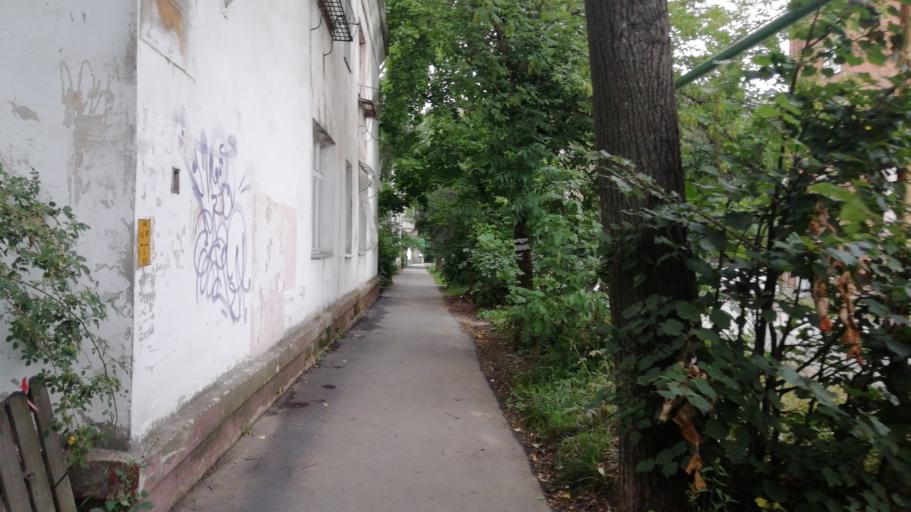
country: RU
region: Tula
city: Mendeleyevskiy
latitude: 54.1638
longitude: 37.5749
